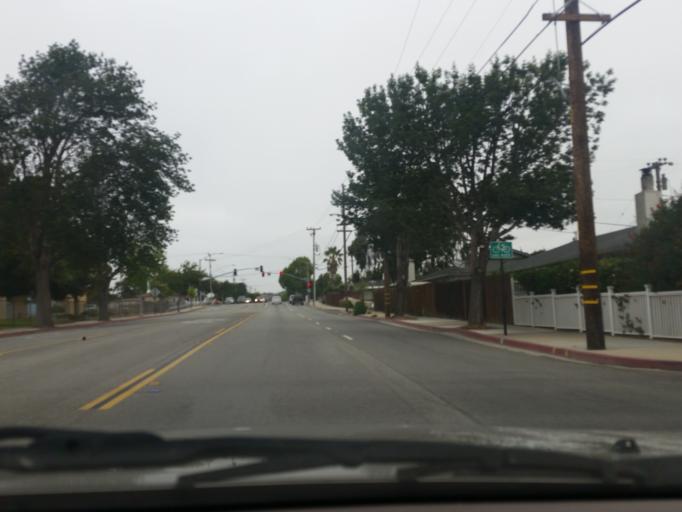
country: US
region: California
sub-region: San Luis Obispo County
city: Arroyo Grande
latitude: 35.1113
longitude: -120.5916
